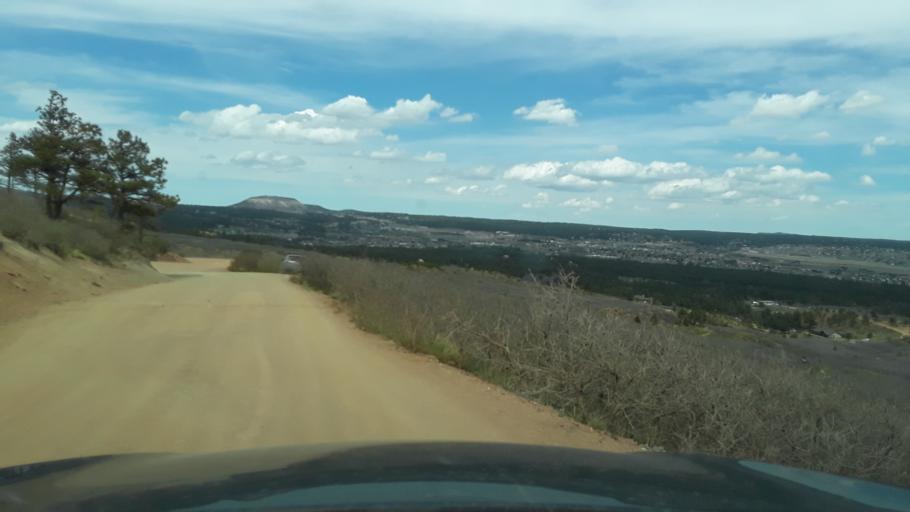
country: US
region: Colorado
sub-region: El Paso County
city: Palmer Lake
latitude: 39.0831
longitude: -104.9129
